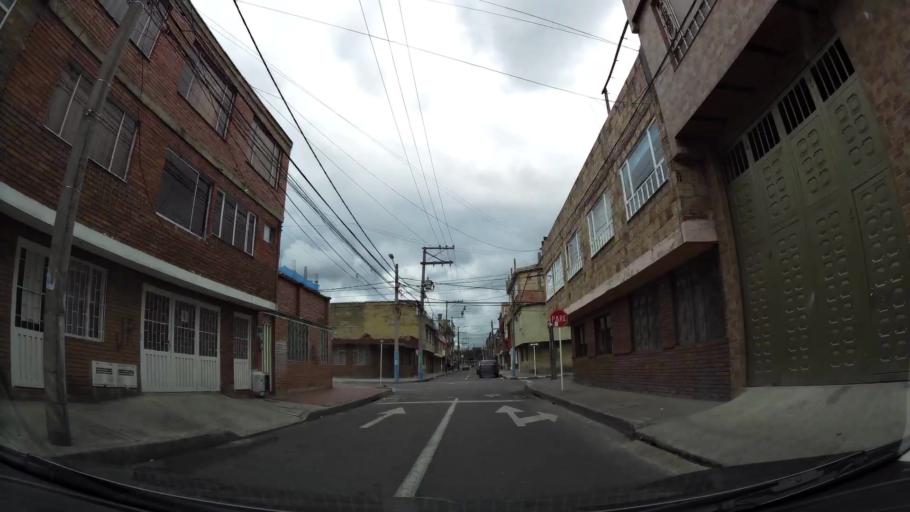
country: CO
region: Bogota D.C.
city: Barrio San Luis
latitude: 4.6967
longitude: -74.0962
